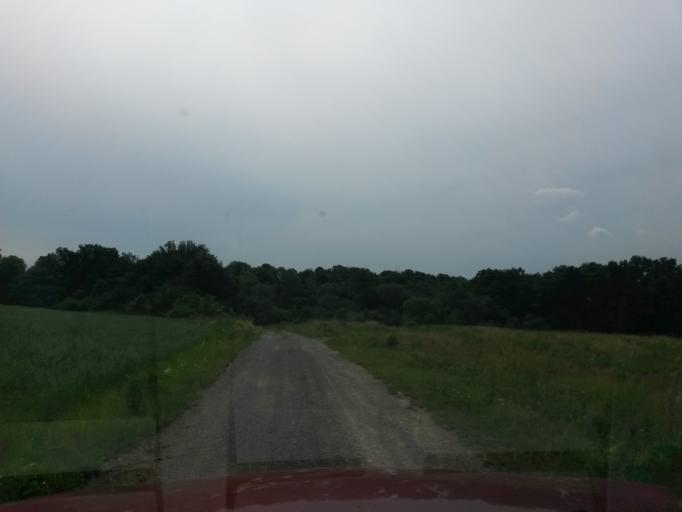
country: SK
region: Kosicky
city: Moldava nad Bodvou
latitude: 48.6717
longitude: 21.1197
